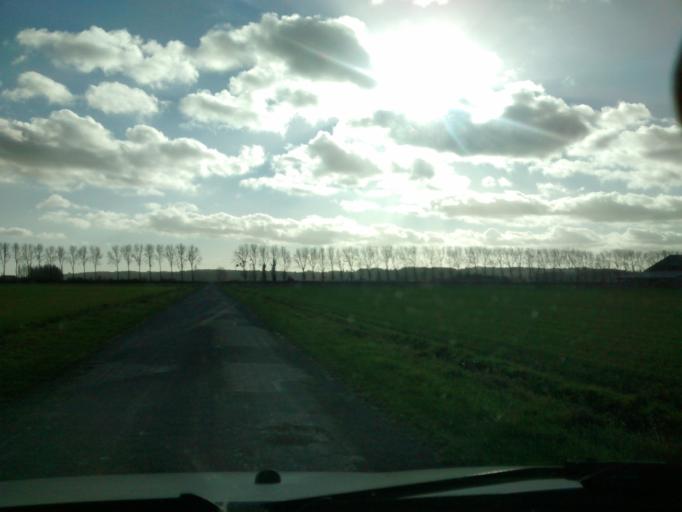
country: FR
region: Brittany
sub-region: Departement d'Ille-et-Vilaine
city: Roz-sur-Couesnon
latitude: 48.6190
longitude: -1.5812
